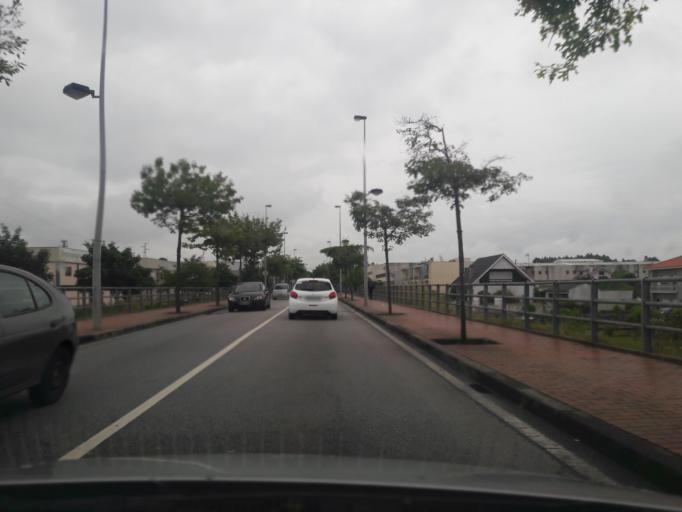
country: PT
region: Porto
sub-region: Vila do Conde
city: Arvore
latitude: 41.3328
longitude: -8.7207
